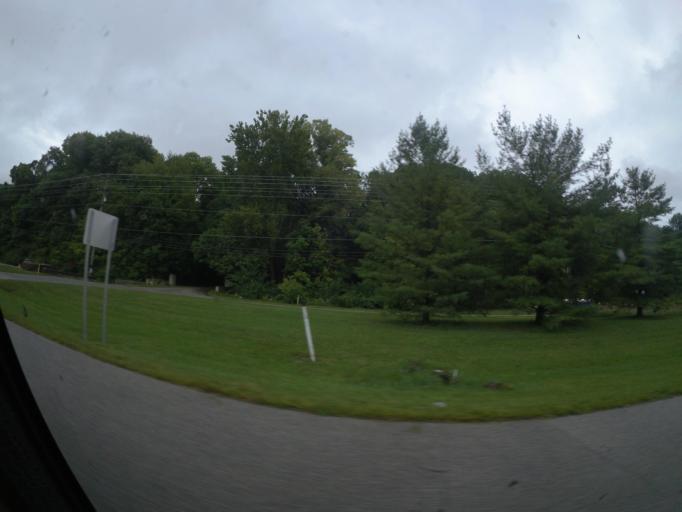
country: US
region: Indiana
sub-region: Montgomery County
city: Crawfordsville
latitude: 40.0557
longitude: -86.9072
